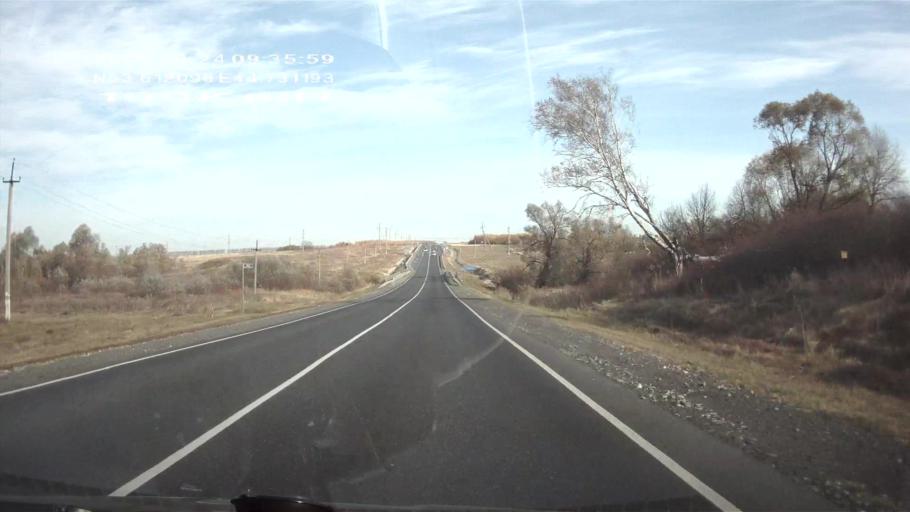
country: RU
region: Penza
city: Mokshan
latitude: 53.6123
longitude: 44.7312
